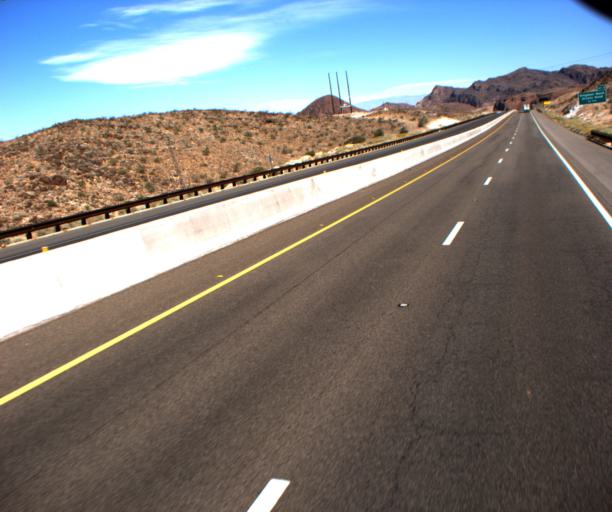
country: US
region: Nevada
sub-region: Clark County
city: Boulder City
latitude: 35.9883
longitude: -114.7150
